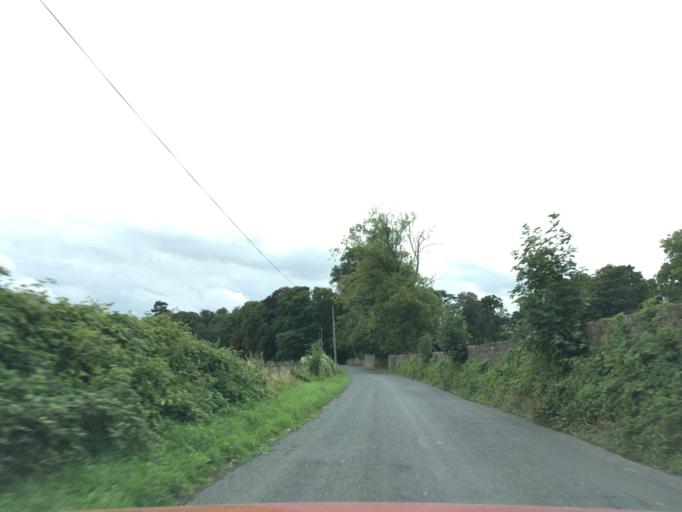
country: GB
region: Wales
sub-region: Monmouthshire
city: Chepstow
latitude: 51.6259
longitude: -2.6858
